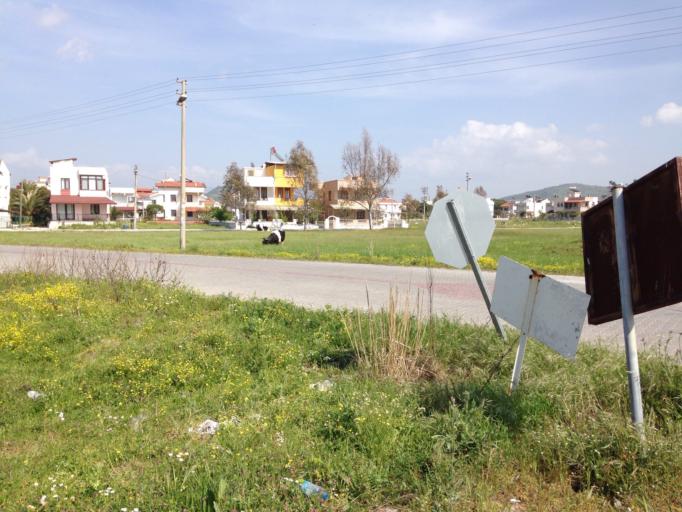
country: TR
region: Izmir
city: Dikili
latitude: 39.0969
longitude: 26.8825
